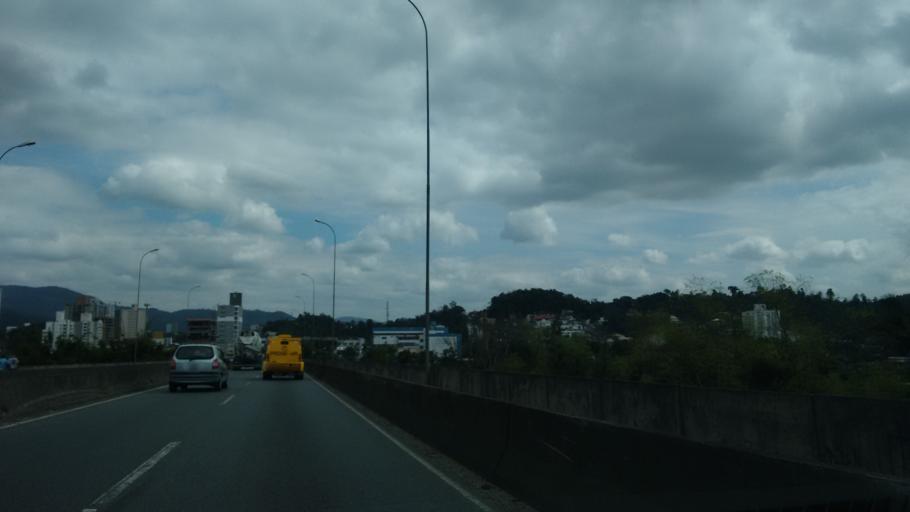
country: BR
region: Santa Catarina
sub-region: Blumenau
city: Blumenau
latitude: -26.8969
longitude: -49.0752
